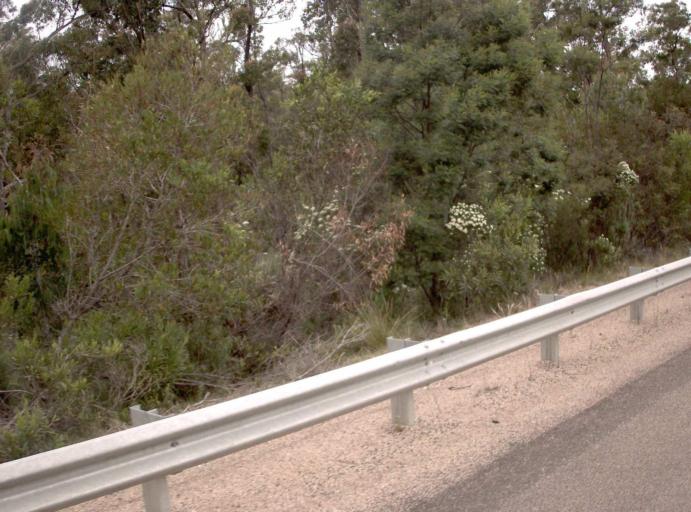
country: AU
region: Victoria
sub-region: East Gippsland
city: Lakes Entrance
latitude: -37.6972
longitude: 148.0484
